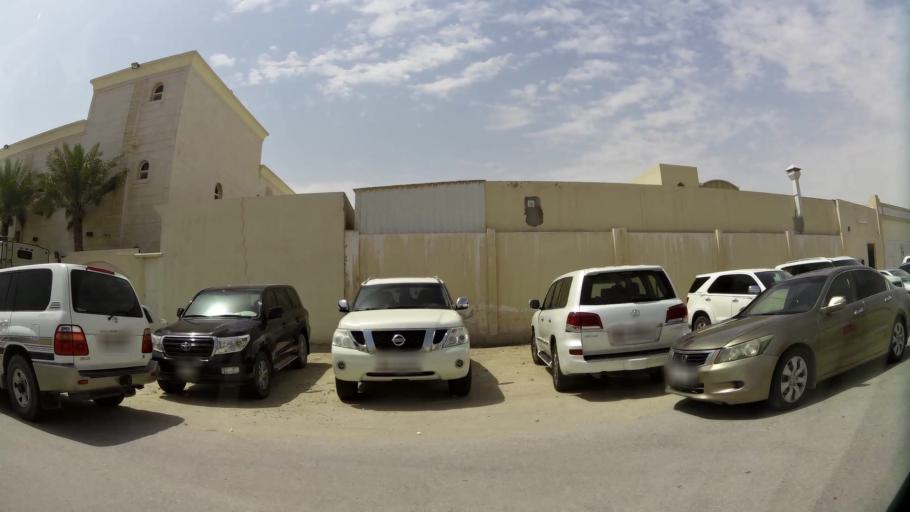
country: QA
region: Baladiyat ar Rayyan
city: Ar Rayyan
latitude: 25.3532
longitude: 51.4764
